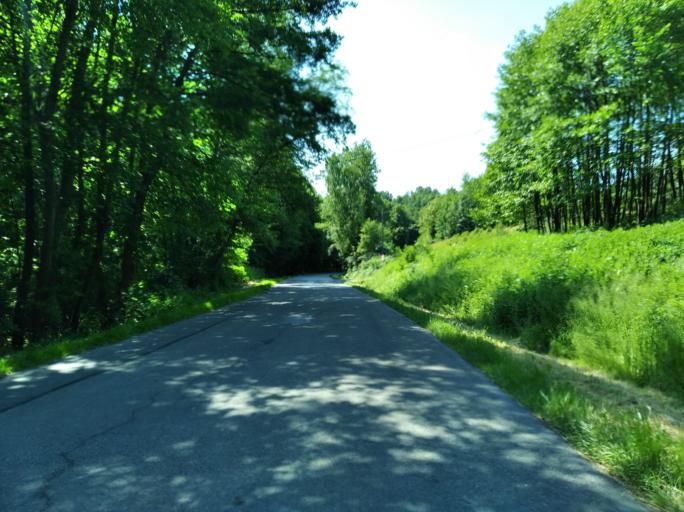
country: PL
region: Subcarpathian Voivodeship
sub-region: Powiat ropczycko-sedziszowski
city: Zagorzyce
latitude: 49.9927
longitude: 21.6473
